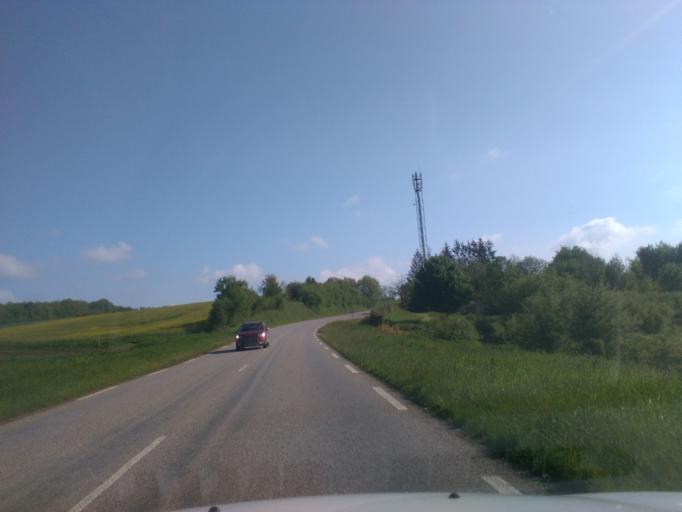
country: FR
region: Lorraine
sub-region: Departement des Vosges
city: Mirecourt
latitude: 48.3289
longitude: 6.1332
